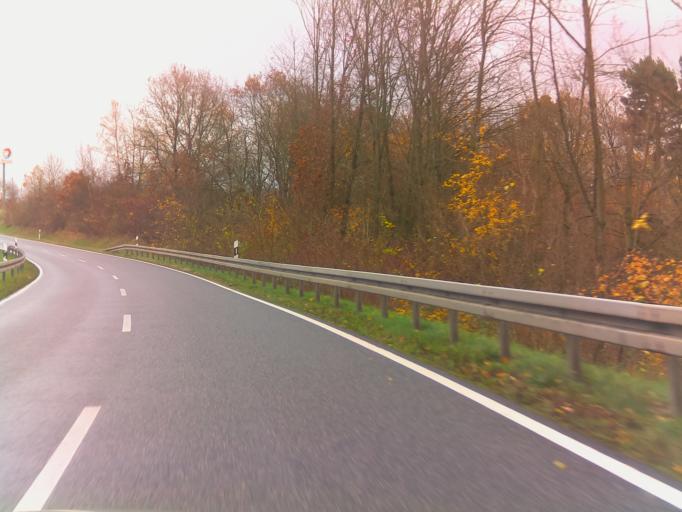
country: DE
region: Thuringia
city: Dankmarshausen
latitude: 50.9570
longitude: 10.0184
